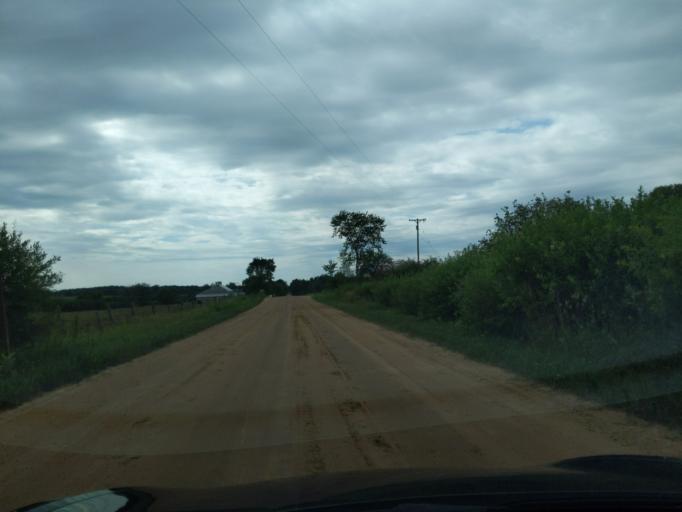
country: US
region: Michigan
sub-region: Clare County
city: Harrison
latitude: 44.0025
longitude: -84.9955
